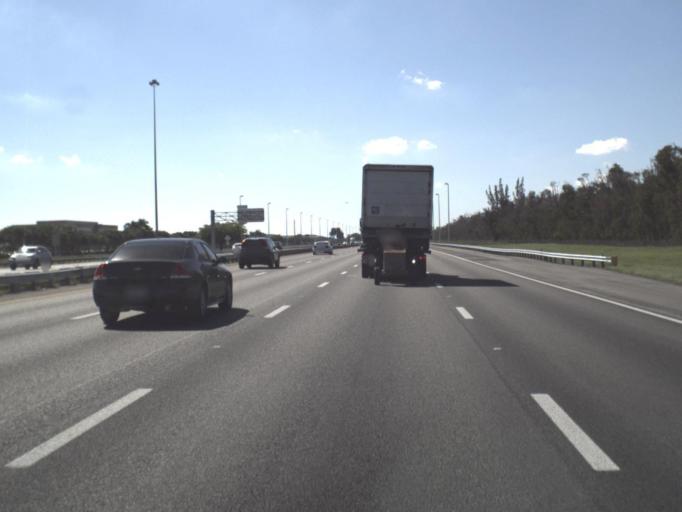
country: US
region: Florida
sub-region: Miami-Dade County
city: Doral
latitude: 25.8677
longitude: -80.3880
